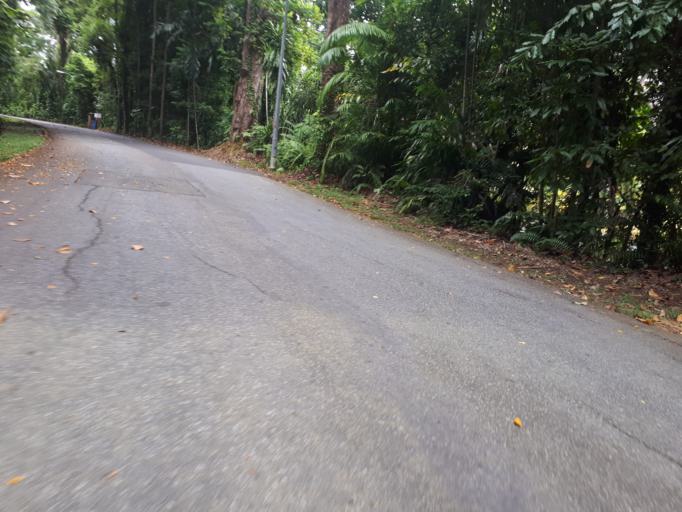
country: SG
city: Singapore
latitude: 1.3133
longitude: 103.8353
